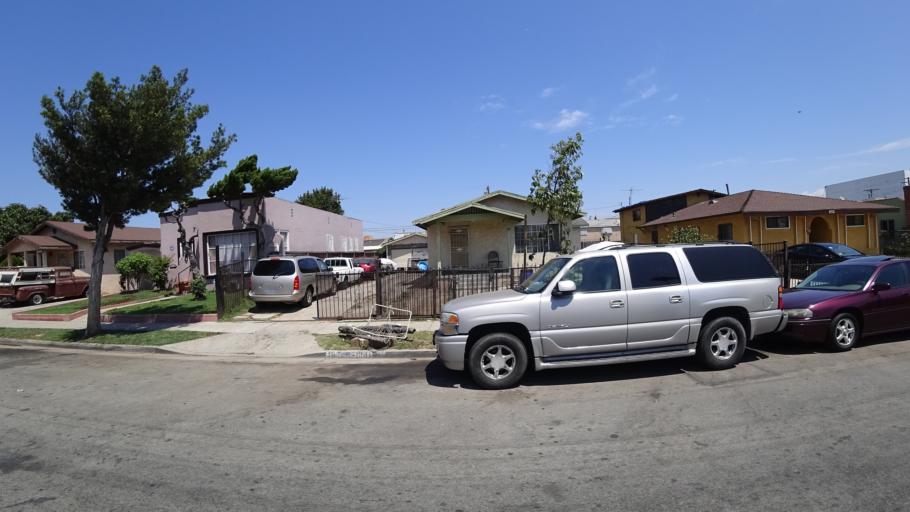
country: US
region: California
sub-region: Los Angeles County
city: Westmont
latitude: 33.9579
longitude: -118.2935
